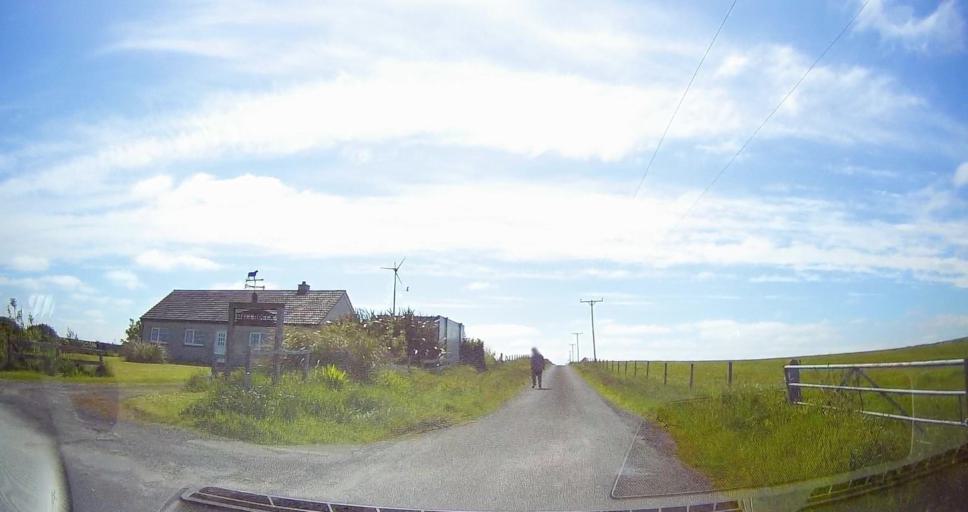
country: GB
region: Scotland
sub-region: Orkney Islands
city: Kirkwall
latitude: 58.8320
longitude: -2.8989
